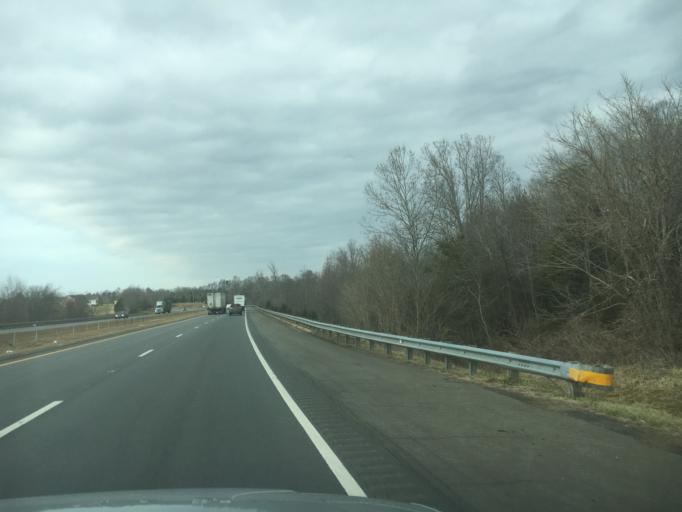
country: US
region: North Carolina
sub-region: Catawba County
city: Maiden
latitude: 35.5484
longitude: -81.2383
